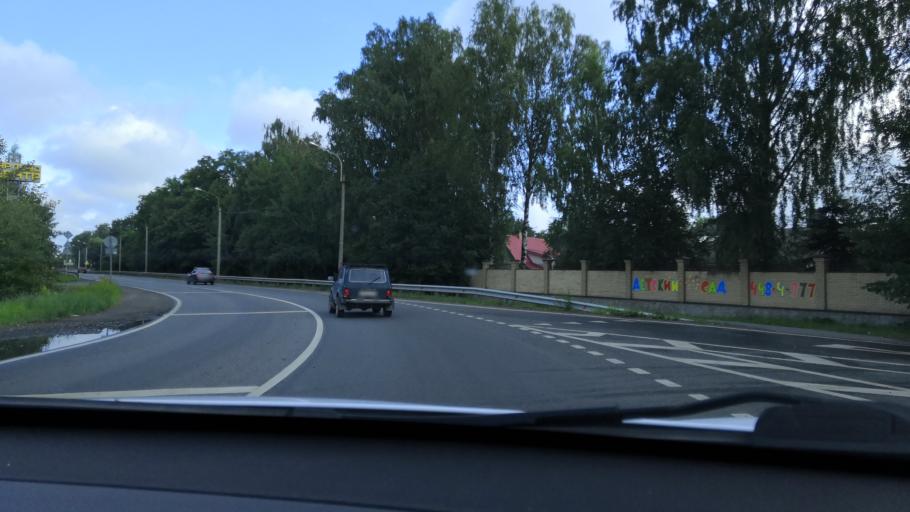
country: RU
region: St.-Petersburg
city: Tyarlevo
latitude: 59.6984
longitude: 30.4415
